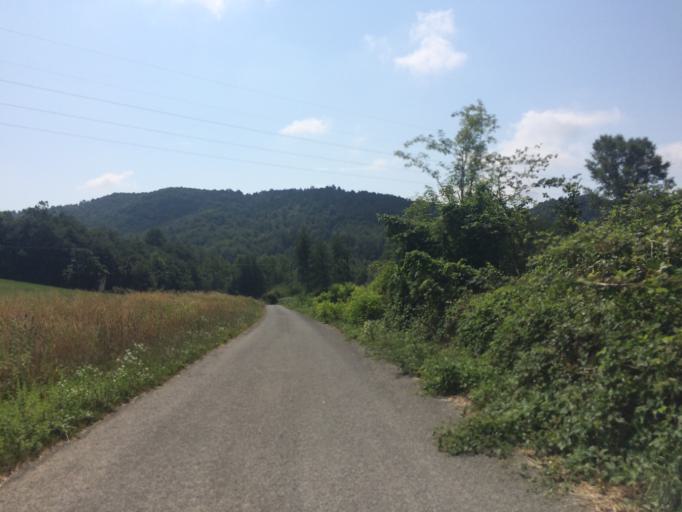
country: IT
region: Piedmont
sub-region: Provincia di Alessandria
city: Pareto
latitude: 44.4977
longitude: 8.3579
